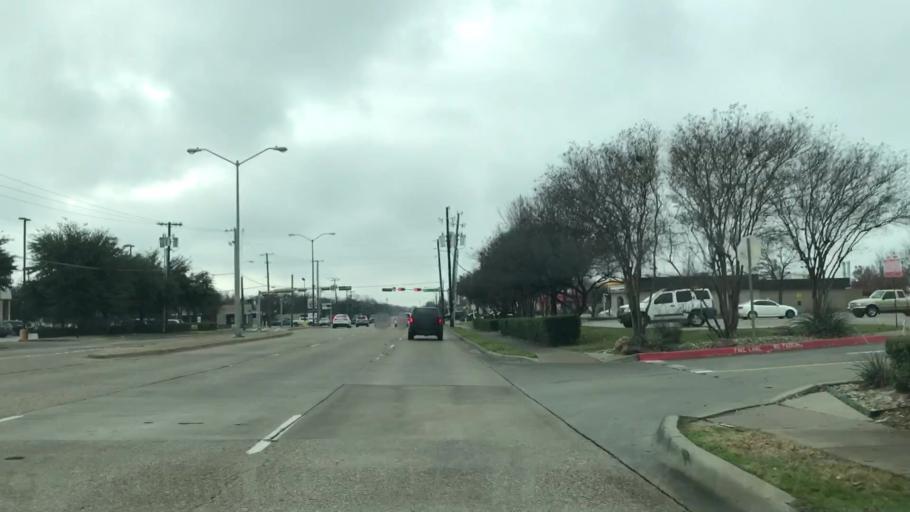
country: US
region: Texas
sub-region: Dallas County
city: Garland
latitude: 32.8655
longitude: -96.6833
